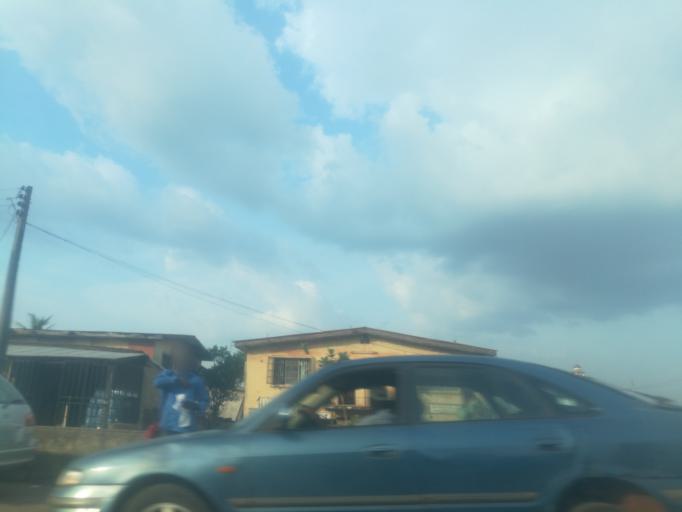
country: NG
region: Ogun
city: Abeokuta
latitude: 7.1632
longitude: 3.3143
